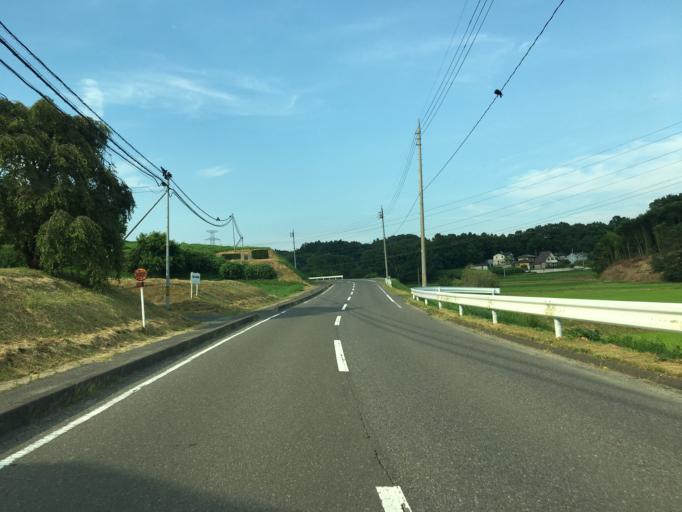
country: JP
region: Fukushima
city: Motomiya
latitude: 37.4987
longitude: 140.4325
